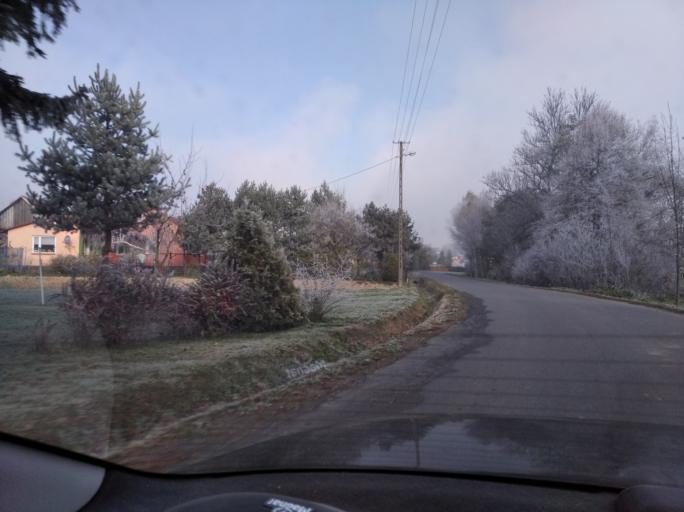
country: PL
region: Subcarpathian Voivodeship
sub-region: Powiat strzyzowski
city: Wysoka Strzyzowska
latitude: 49.8481
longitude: 21.7309
